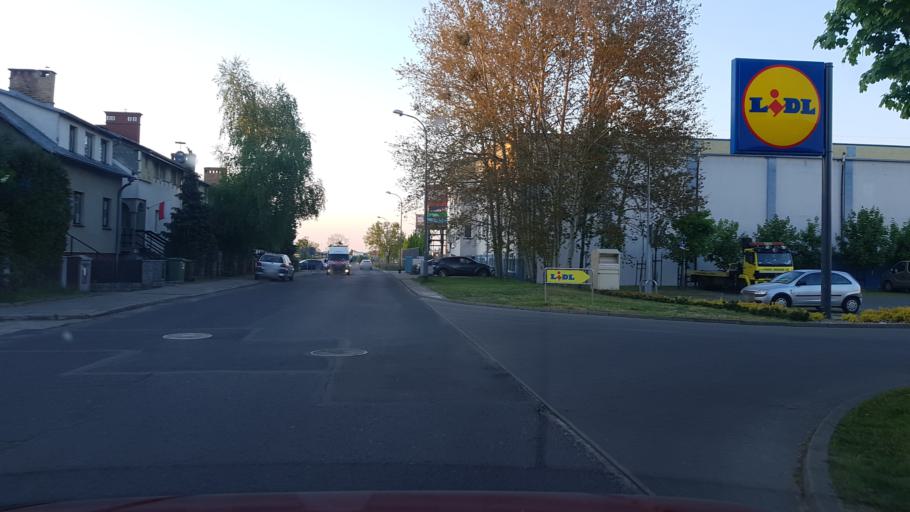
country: PL
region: West Pomeranian Voivodeship
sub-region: Szczecin
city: Szczecin
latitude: 53.3788
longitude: 14.6684
